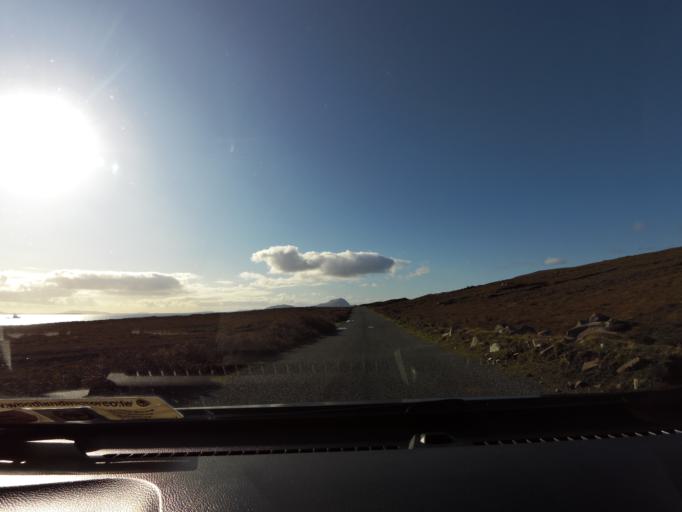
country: IE
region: Connaught
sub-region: Maigh Eo
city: Westport
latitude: 53.8753
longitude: -9.8324
